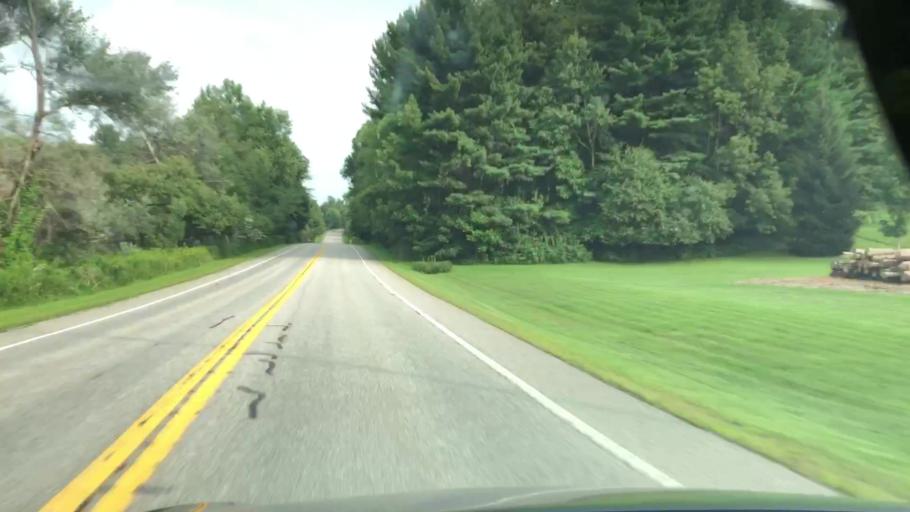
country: US
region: Pennsylvania
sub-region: Erie County
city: Union City
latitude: 42.0543
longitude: -79.8516
